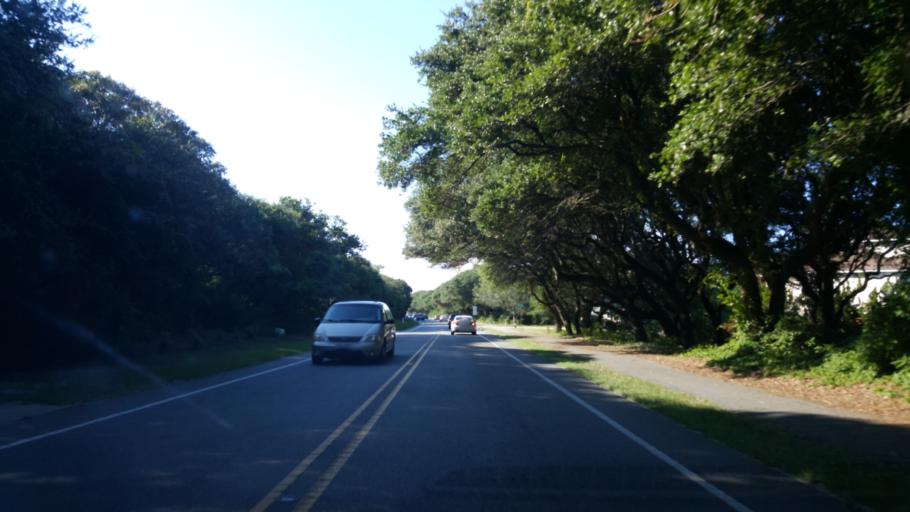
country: US
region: North Carolina
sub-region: Dare County
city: Southern Shores
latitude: 36.1387
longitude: -75.7364
